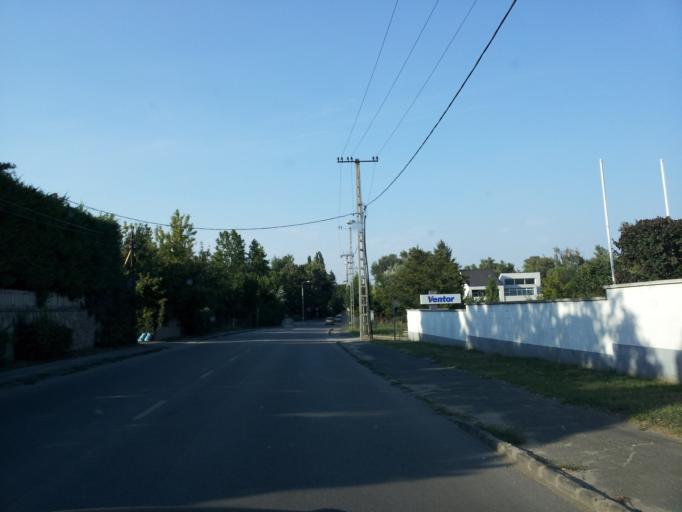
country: HU
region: Pest
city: Szentendre
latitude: 47.6893
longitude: 19.0859
